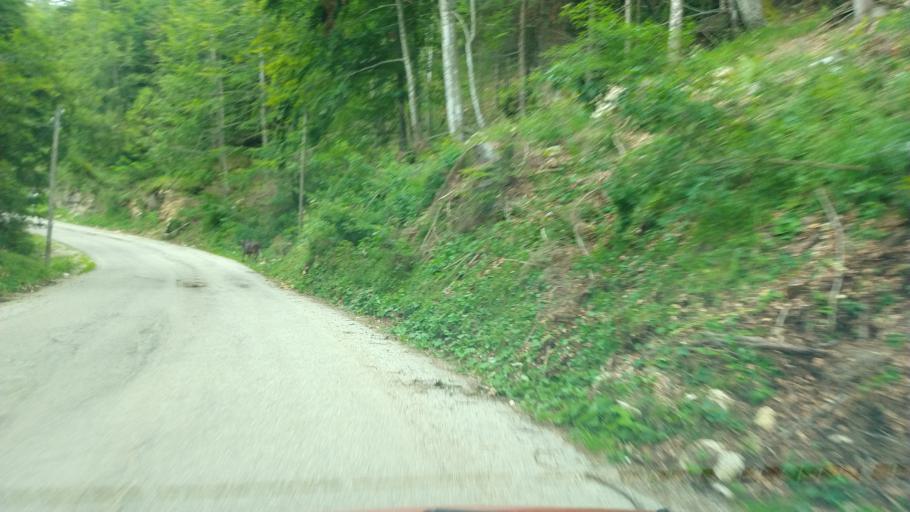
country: IT
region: Veneto
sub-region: Provincia di Vicenza
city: Pedemonte
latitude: 45.8819
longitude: 11.2940
